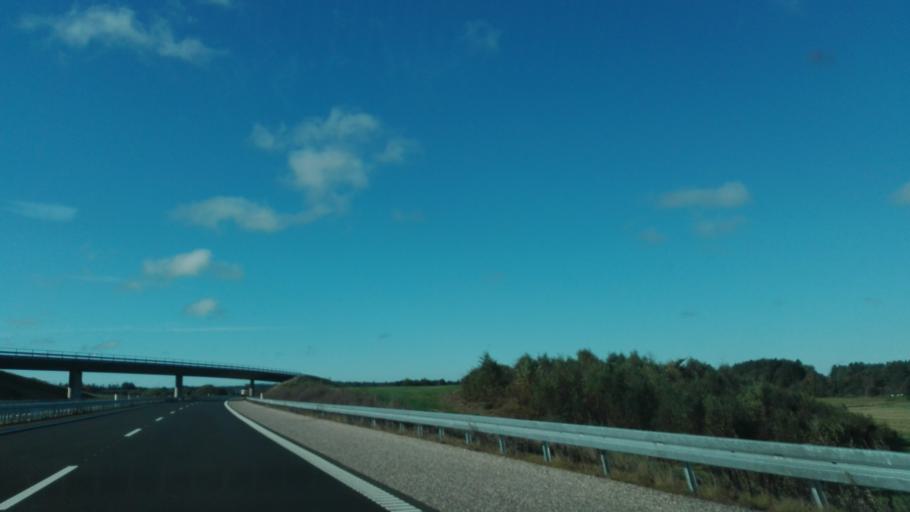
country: DK
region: Central Jutland
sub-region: Silkeborg Kommune
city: Silkeborg
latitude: 56.1490
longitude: 9.4467
